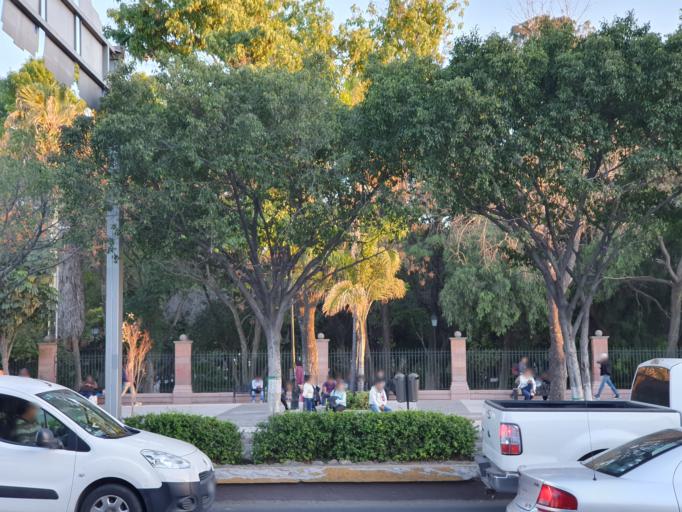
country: MX
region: Queretaro
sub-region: Queretaro
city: Santiago de Queretaro
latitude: 20.5897
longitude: -100.3882
